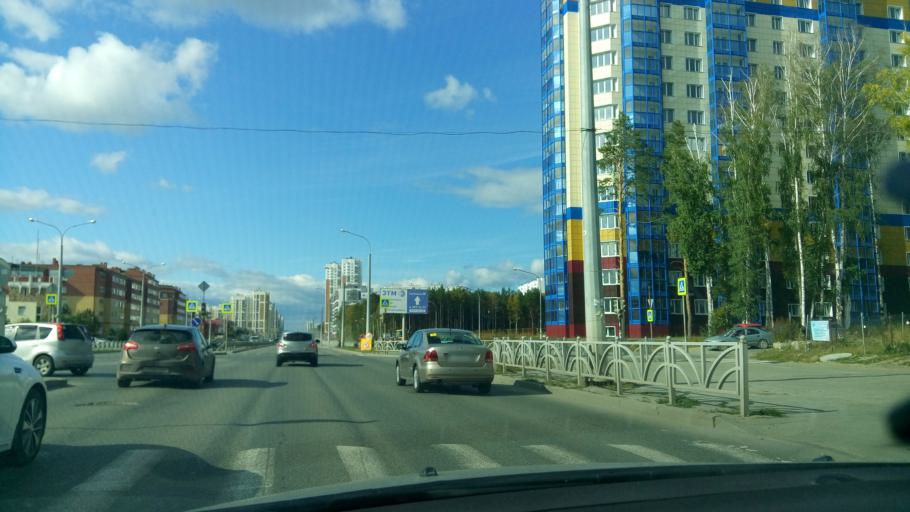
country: RU
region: Sverdlovsk
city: Sovkhoznyy
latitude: 56.7829
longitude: 60.5401
